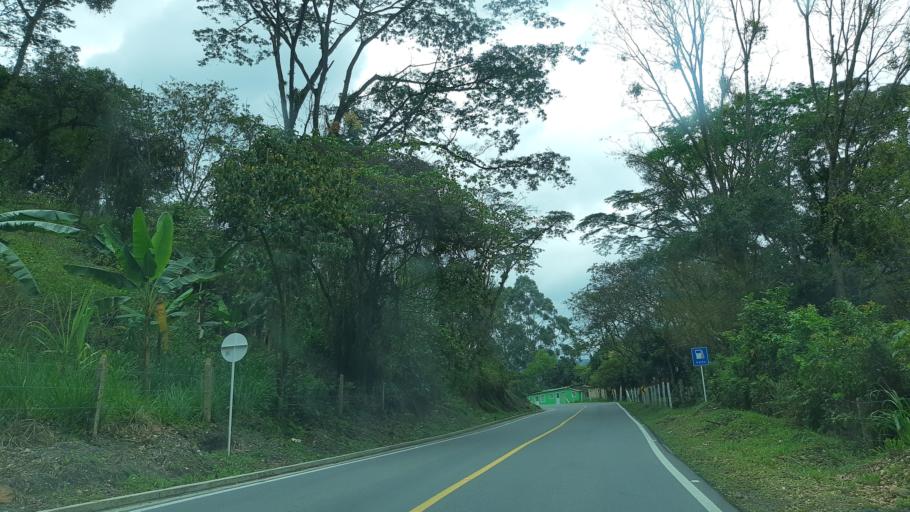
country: CO
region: Boyaca
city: Somondoco
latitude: 4.9819
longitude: -73.3431
